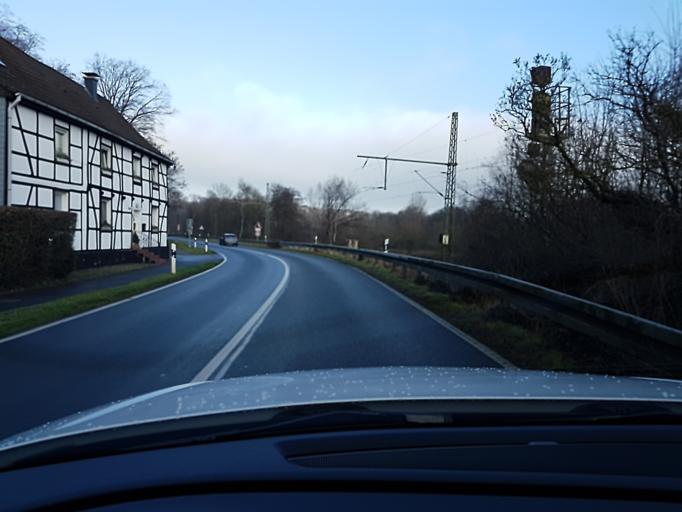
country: DE
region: North Rhine-Westphalia
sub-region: Regierungsbezirk Dusseldorf
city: Heiligenhaus
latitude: 51.3706
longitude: 6.9611
